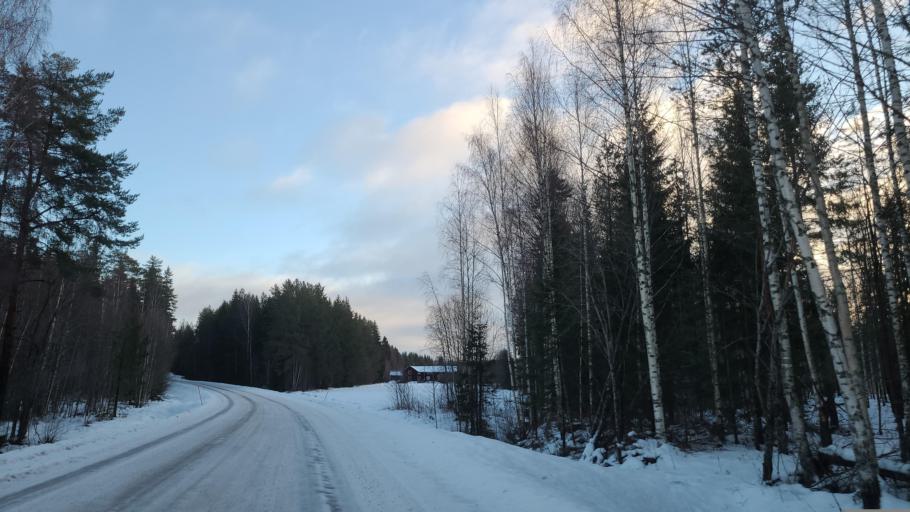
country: SE
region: Gaevleborg
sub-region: Bollnas Kommun
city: Bollnas
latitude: 61.3893
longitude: 16.4211
